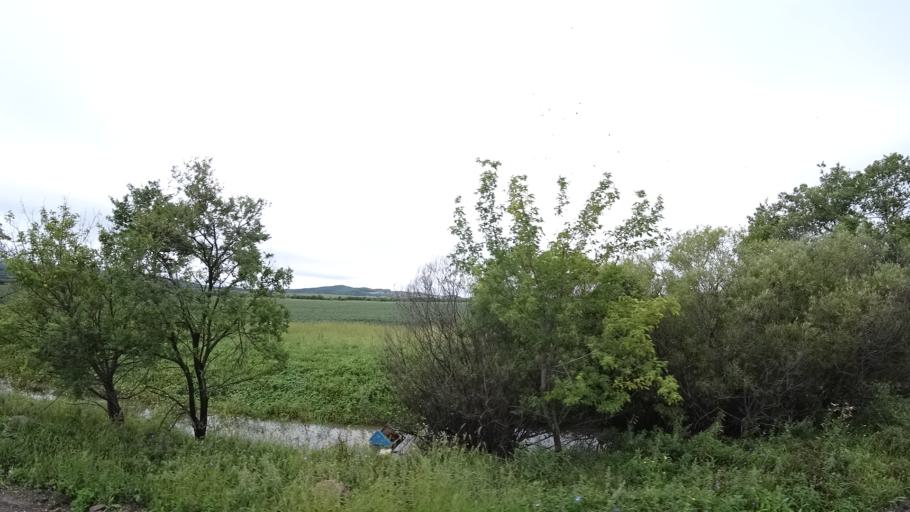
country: RU
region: Primorskiy
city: Monastyrishche
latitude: 44.1830
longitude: 132.4836
